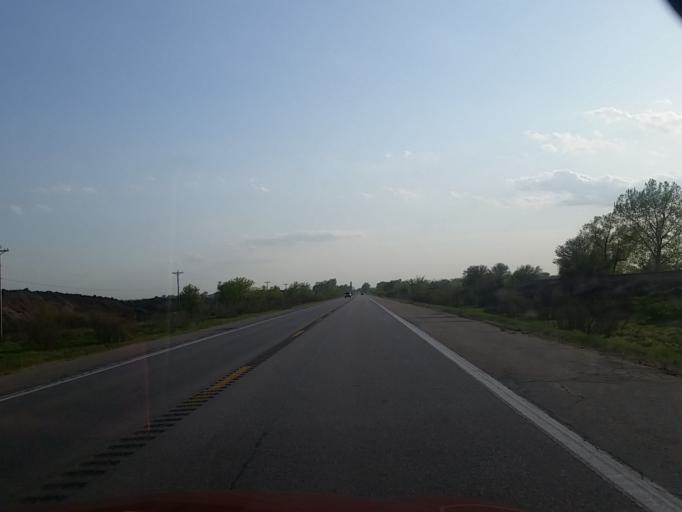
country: US
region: Nebraska
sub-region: Saunders County
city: Ashland
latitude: 41.0738
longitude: -96.3051
